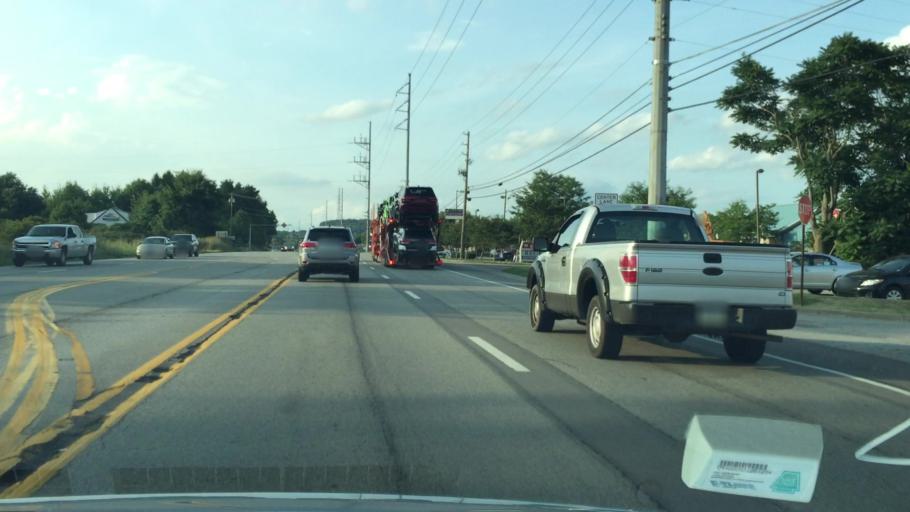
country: US
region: Pennsylvania
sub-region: Butler County
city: Cranberry Township
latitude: 40.7046
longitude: -80.1043
